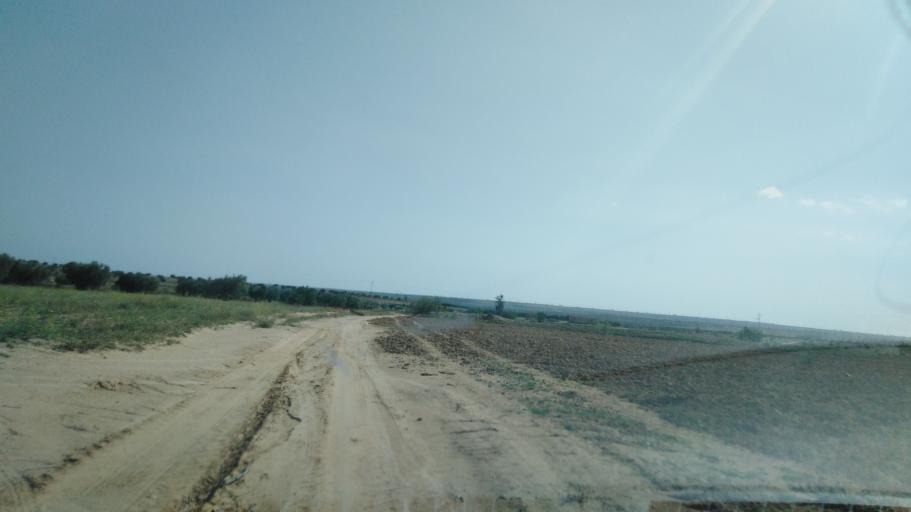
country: TN
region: Safaqis
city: Bi'r `Ali Bin Khalifah
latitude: 34.7927
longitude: 10.3719
